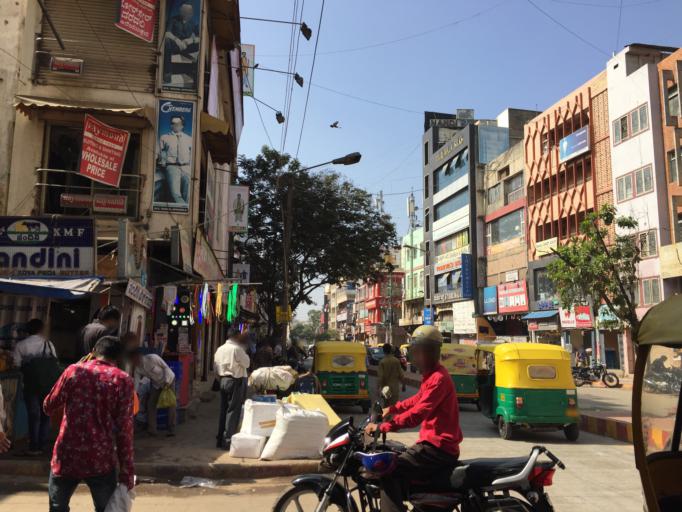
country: IN
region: Karnataka
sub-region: Bangalore Urban
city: Bangalore
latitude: 12.9705
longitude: 77.5760
